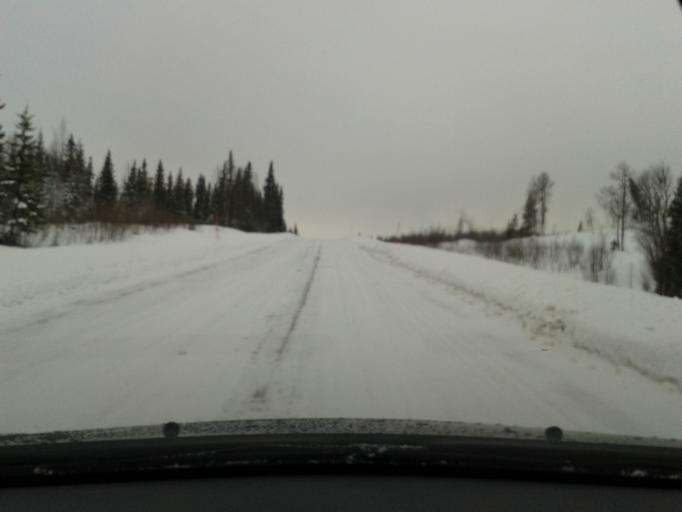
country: SE
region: Vaesterbotten
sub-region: Vilhelmina Kommun
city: Sjoberg
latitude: 65.2028
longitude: 15.9779
